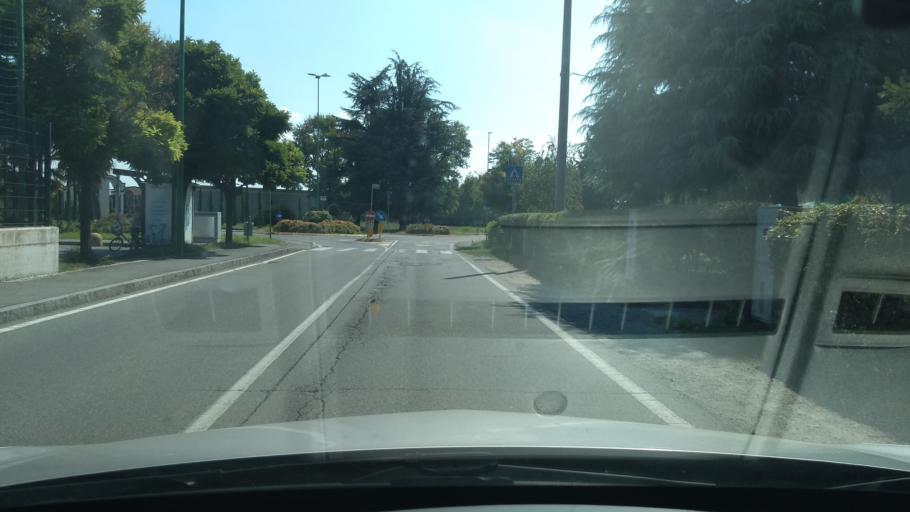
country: IT
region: Lombardy
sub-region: Provincia di Bergamo
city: Ghisalba
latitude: 45.5937
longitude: 9.7509
